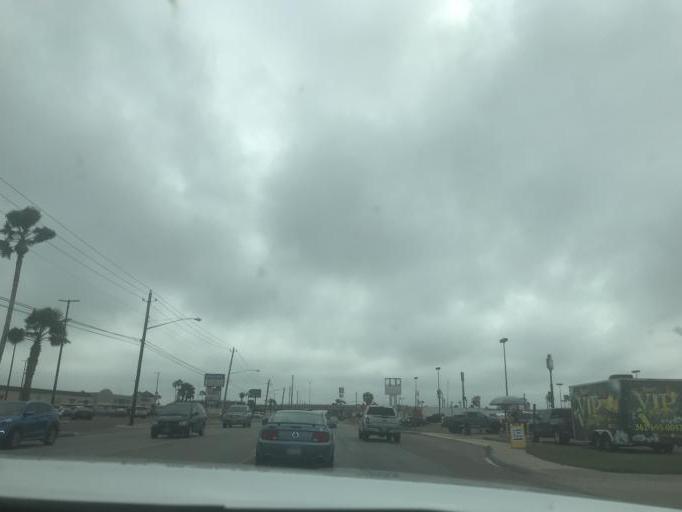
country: US
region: Texas
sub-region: Nueces County
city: Corpus Christi
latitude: 27.7072
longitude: -97.3627
